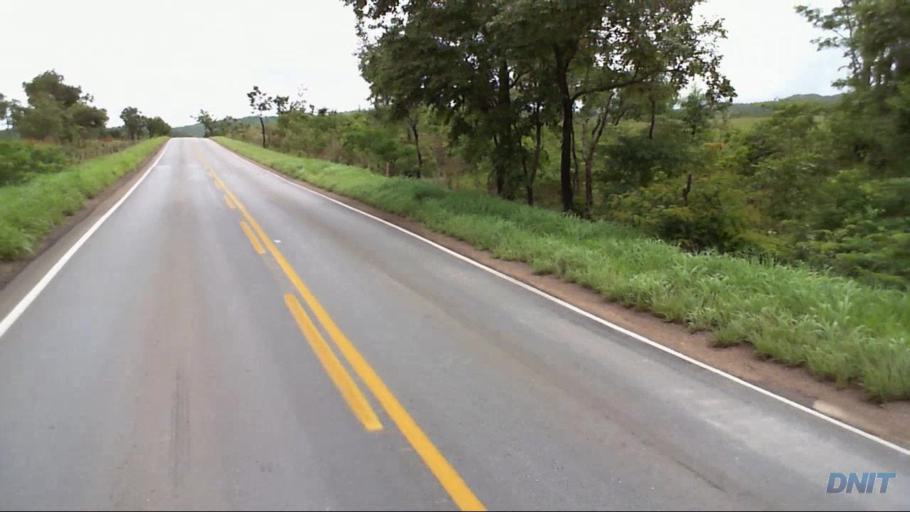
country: BR
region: Goias
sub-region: Padre Bernardo
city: Padre Bernardo
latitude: -15.4476
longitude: -48.2046
